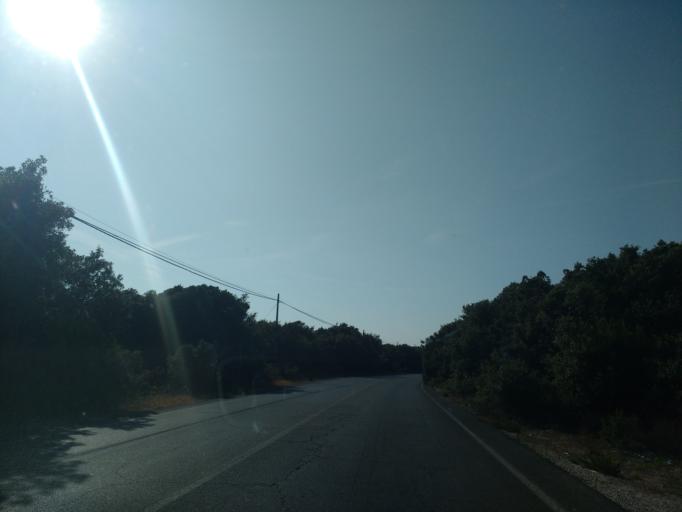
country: IT
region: Latium
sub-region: Citta metropolitana di Roma Capitale
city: Acilia-Castel Fusano-Ostia Antica
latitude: 41.6975
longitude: 12.3570
